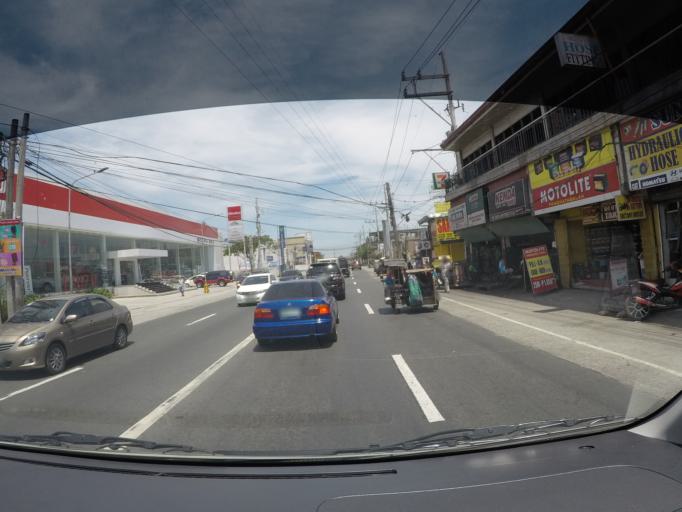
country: PH
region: Calabarzon
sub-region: Province of Laguna
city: Pulong Santa Cruz
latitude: 14.2775
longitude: 121.0835
